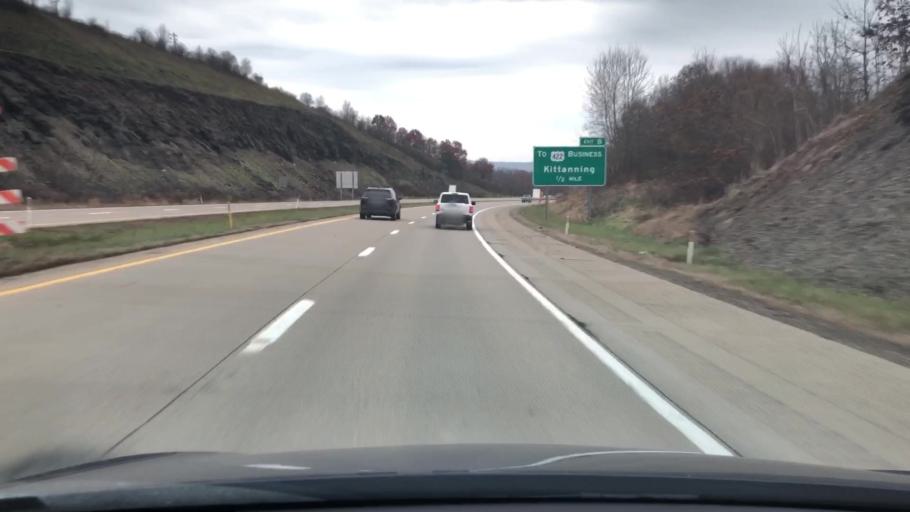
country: US
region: Pennsylvania
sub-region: Armstrong County
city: Kittanning
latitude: 40.7953
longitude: -79.4953
